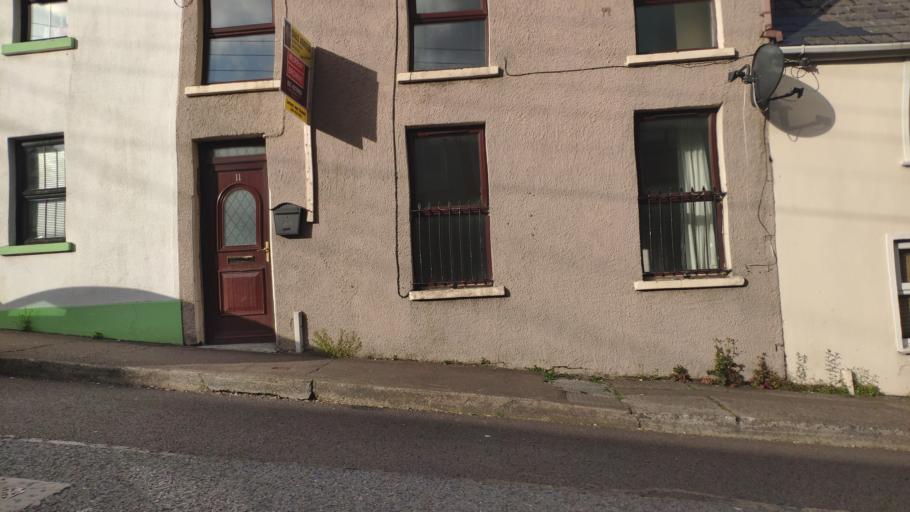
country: IE
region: Munster
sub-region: County Cork
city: Cork
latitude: 51.9072
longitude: -8.4821
